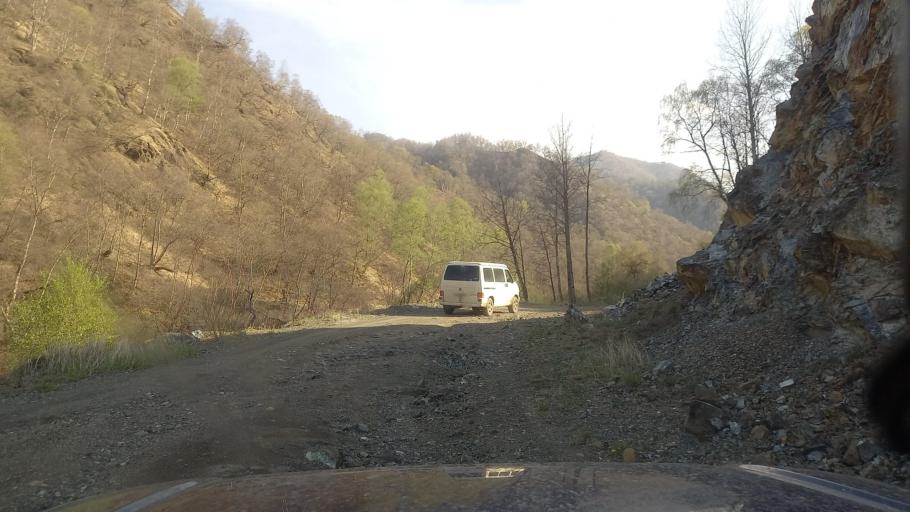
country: RU
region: Kabardino-Balkariya
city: Kamennomostskoye
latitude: 43.7006
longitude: 42.8431
